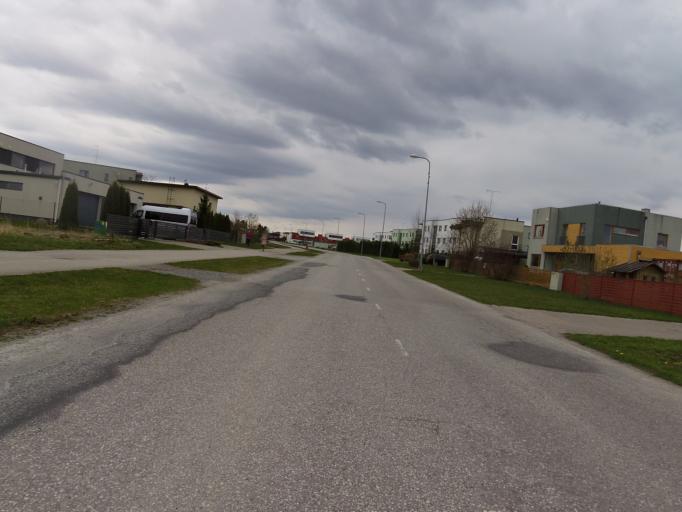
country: EE
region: Harju
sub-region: Tallinna linn
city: Tallinn
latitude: 59.3960
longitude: 24.8031
